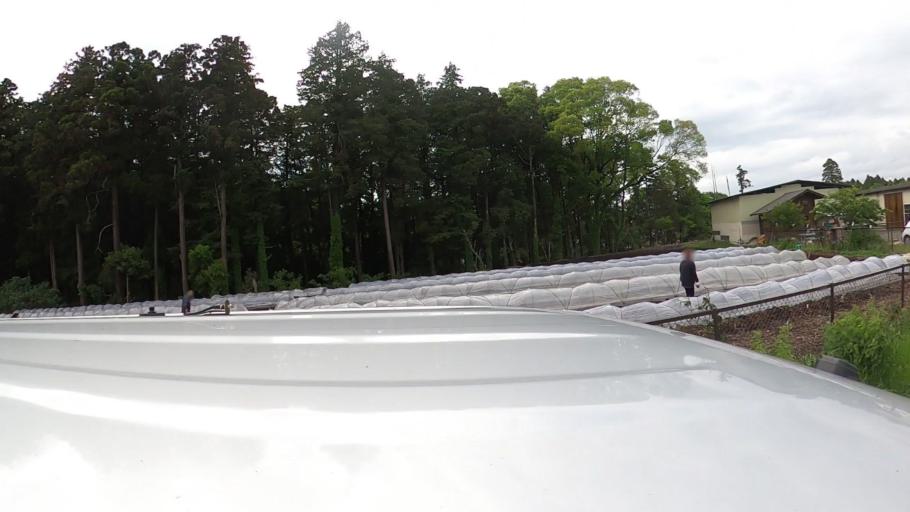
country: JP
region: Ibaraki
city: Edosaki
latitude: 35.9895
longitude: 140.2579
